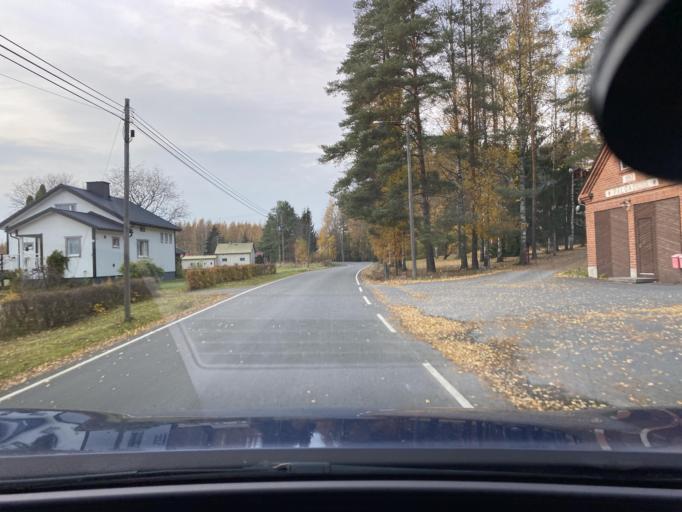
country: FI
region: Varsinais-Suomi
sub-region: Loimaa
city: Alastaro
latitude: 61.0870
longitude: 22.9152
